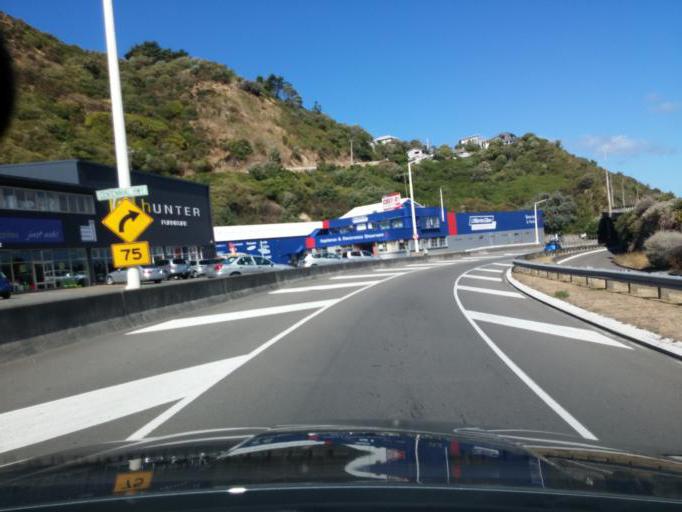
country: NZ
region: Wellington
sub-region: Wellington City
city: Wellington
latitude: -41.2428
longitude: 174.8136
